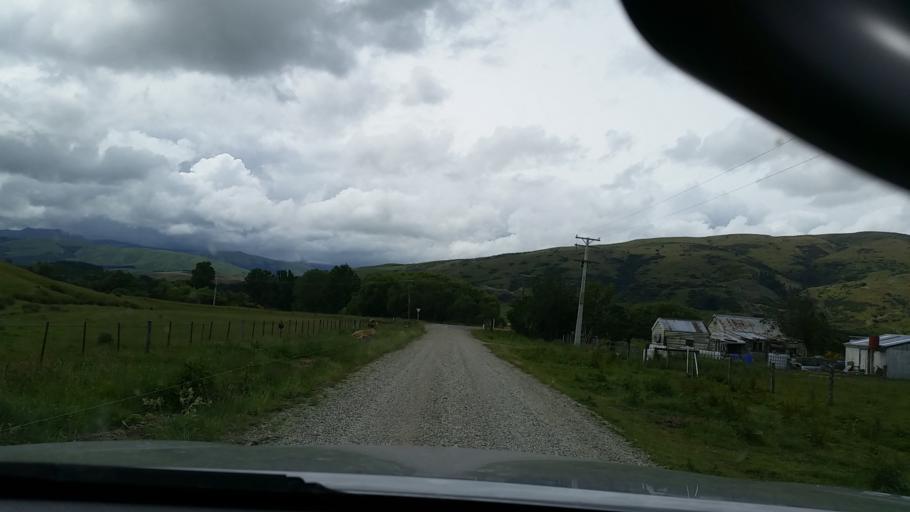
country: NZ
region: Southland
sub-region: Gore District
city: Gore
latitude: -45.7339
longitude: 168.8236
